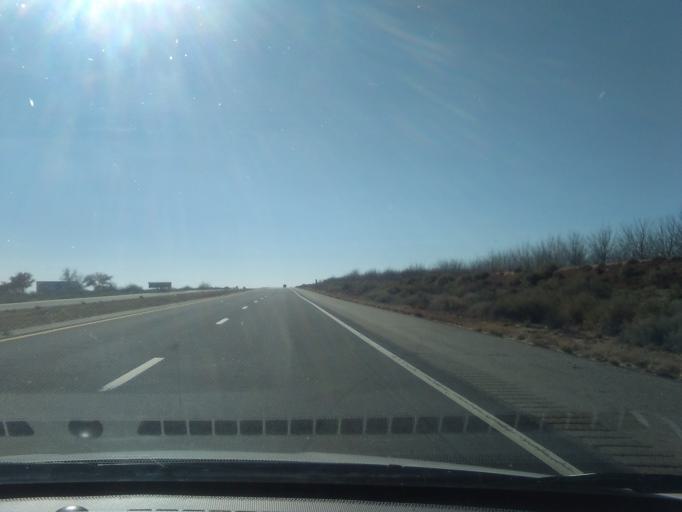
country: US
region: New Mexico
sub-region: Valencia County
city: Jarales
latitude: 34.6007
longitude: -106.7878
